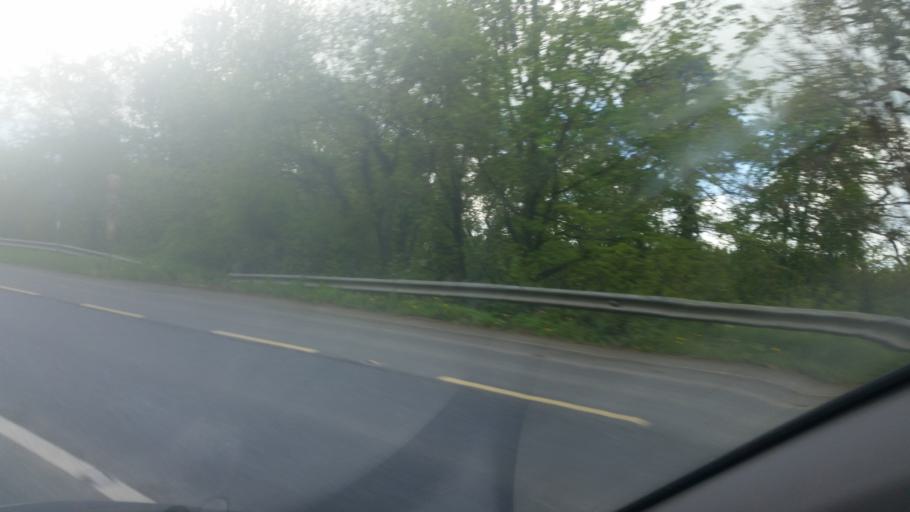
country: IE
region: Leinster
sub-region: Loch Garman
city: Enniscorthy
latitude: 52.4900
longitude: -6.5660
